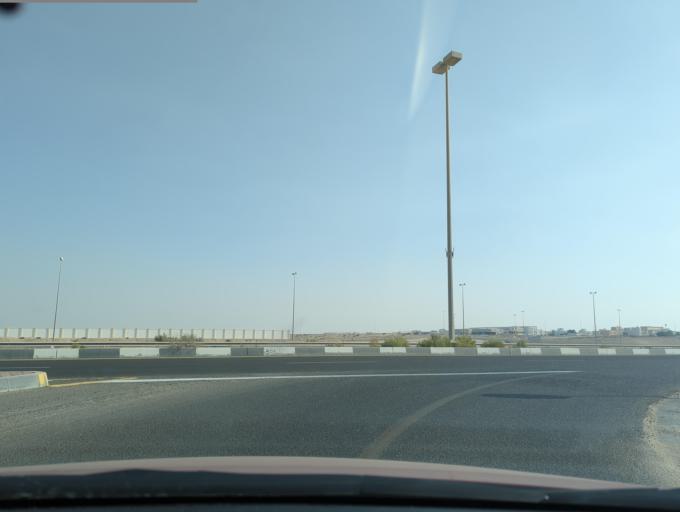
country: AE
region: Abu Dhabi
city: Abu Dhabi
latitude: 24.3935
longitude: 54.7435
